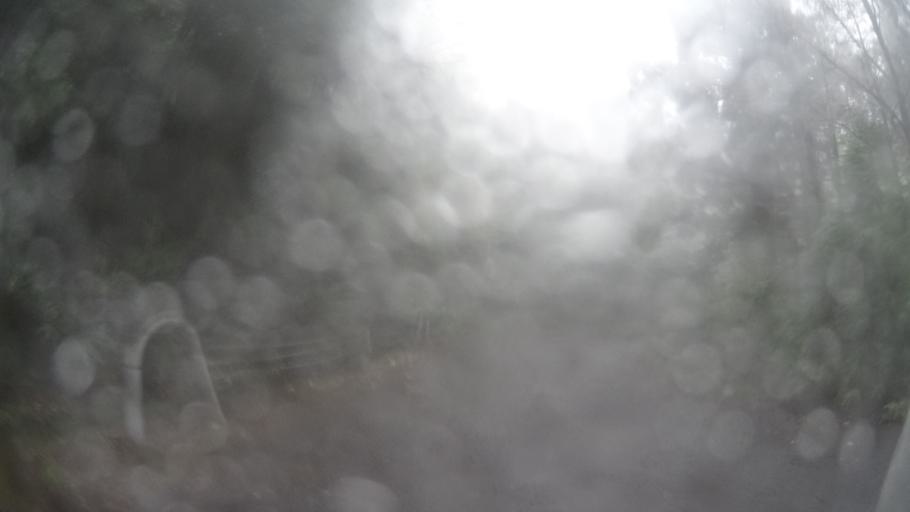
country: JP
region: Kagoshima
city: Nishinoomote
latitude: 30.3006
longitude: 130.5553
